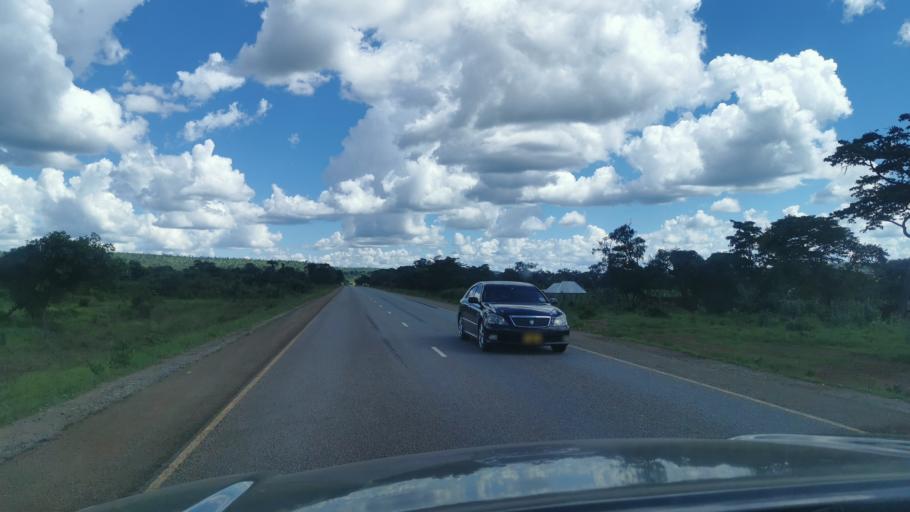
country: TZ
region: Geita
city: Uyovu
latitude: -3.0940
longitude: 31.2988
